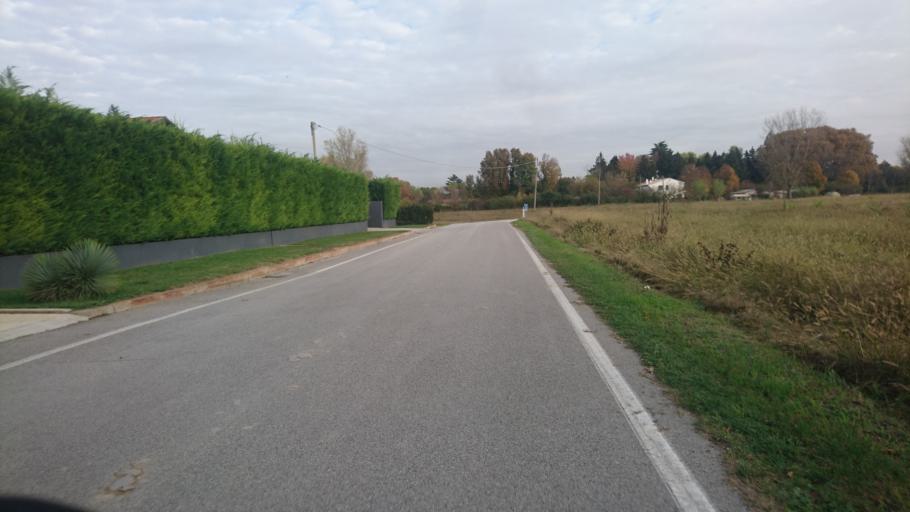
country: IT
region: Veneto
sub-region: Provincia di Padova
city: Mandriola-Sant'Agostino
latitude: 45.3817
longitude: 11.8392
